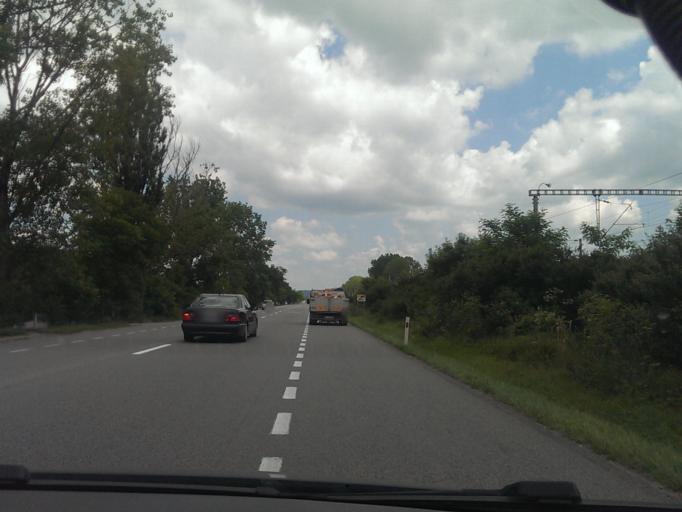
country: RO
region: Cluj
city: Jucu Herghelia
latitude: 46.8663
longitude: 23.7658
